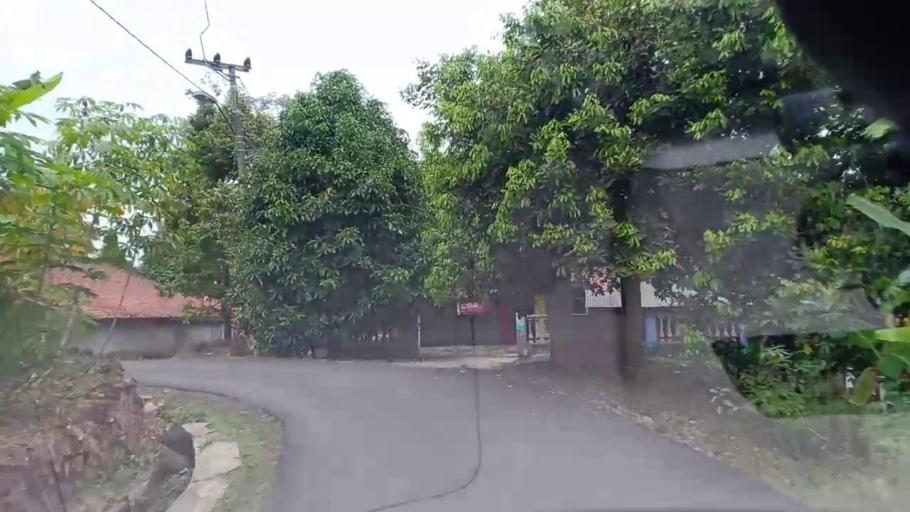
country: ID
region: West Java
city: Gerempay
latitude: -7.3373
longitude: 108.2943
